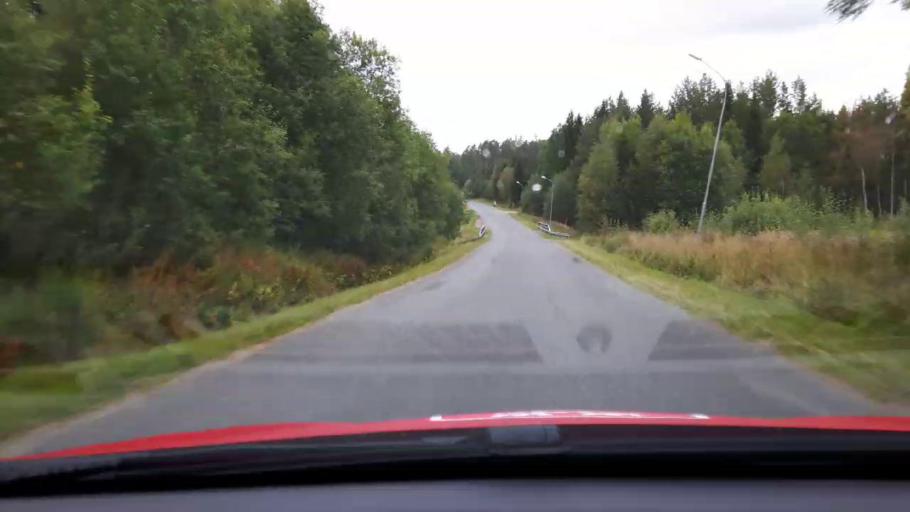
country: SE
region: Jaemtland
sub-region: Bergs Kommun
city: Hoverberg
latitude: 62.8558
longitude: 14.3288
